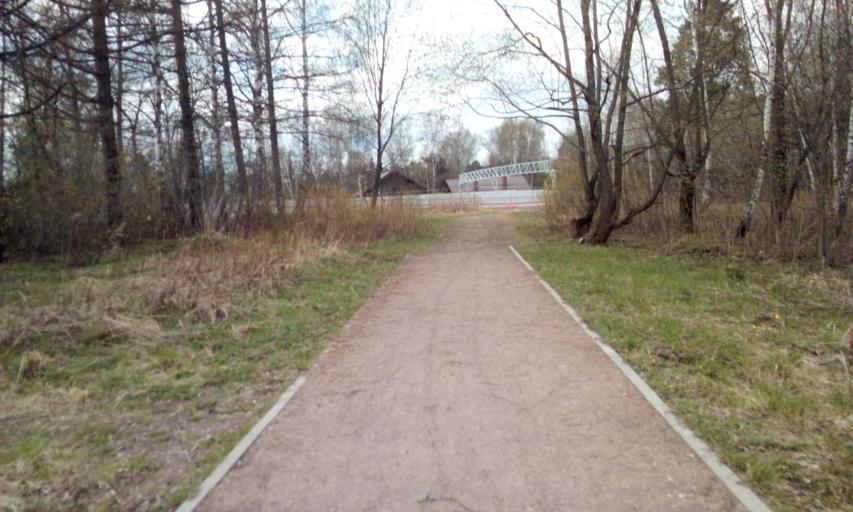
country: RU
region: Moscow
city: Novo-Peredelkino
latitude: 55.6480
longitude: 37.3342
